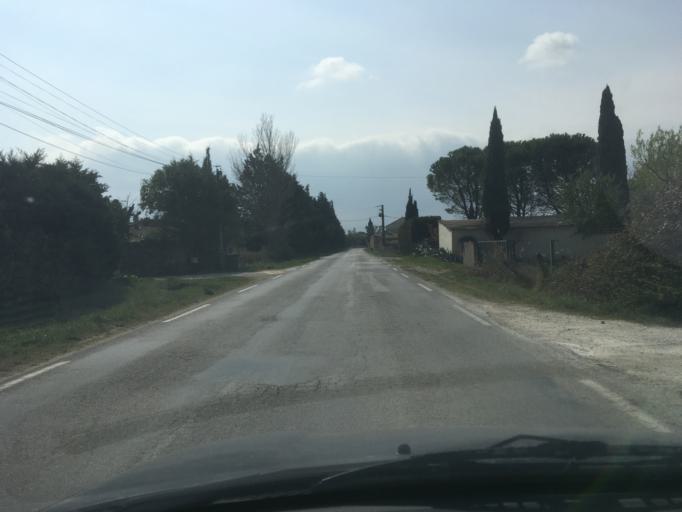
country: FR
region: Provence-Alpes-Cote d'Azur
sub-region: Departement du Vaucluse
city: Sarrians
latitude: 44.0893
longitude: 4.9843
